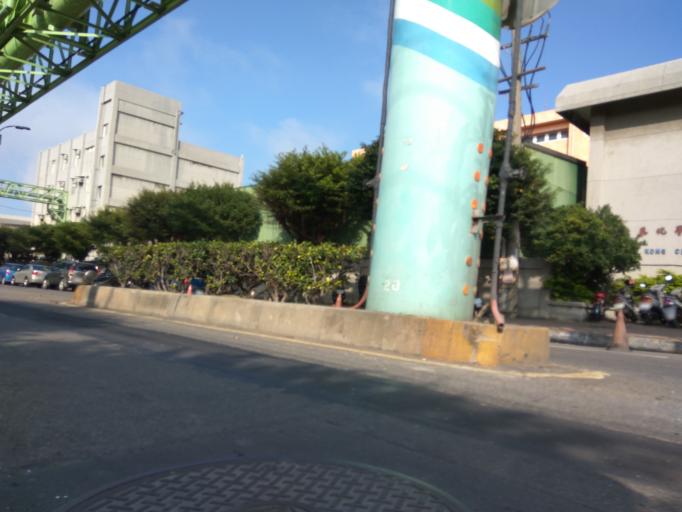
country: TW
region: Taiwan
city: Taoyuan City
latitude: 25.0748
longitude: 121.1762
